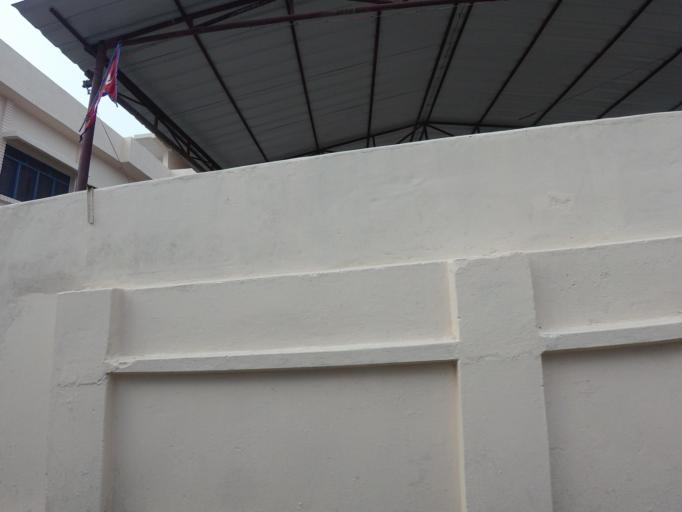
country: NP
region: Western Region
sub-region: Lumbini Zone
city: Bhairahawa
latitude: 27.5235
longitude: 83.4548
